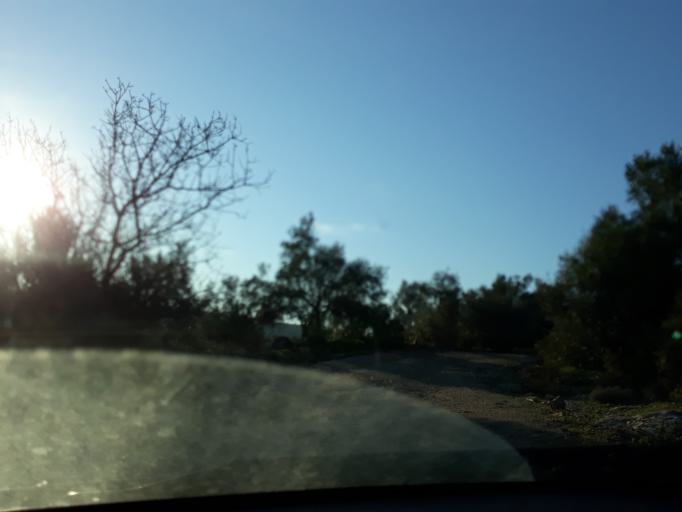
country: GR
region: Central Greece
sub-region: Nomos Voiotias
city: Asopia
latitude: 38.2647
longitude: 23.5341
